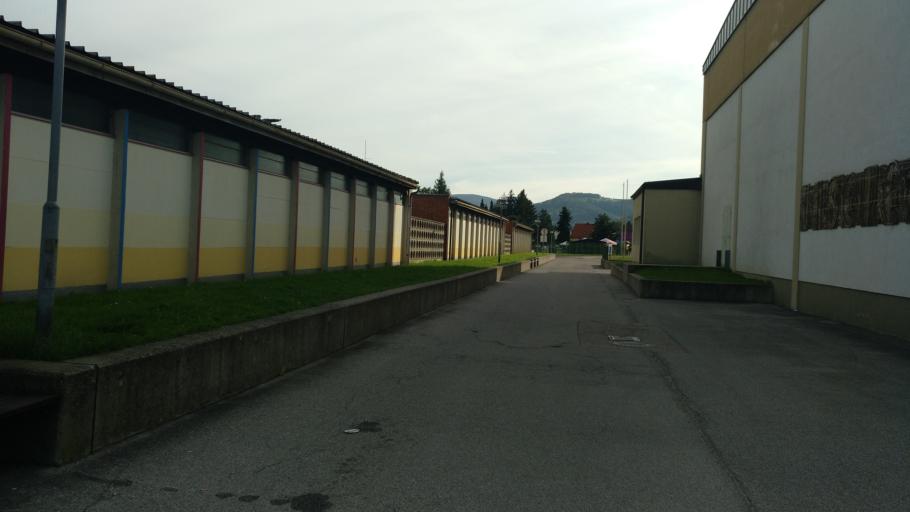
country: AT
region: Lower Austria
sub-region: Politischer Bezirk Sankt Polten
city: Wilhelmsburg
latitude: 48.0997
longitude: 15.6027
